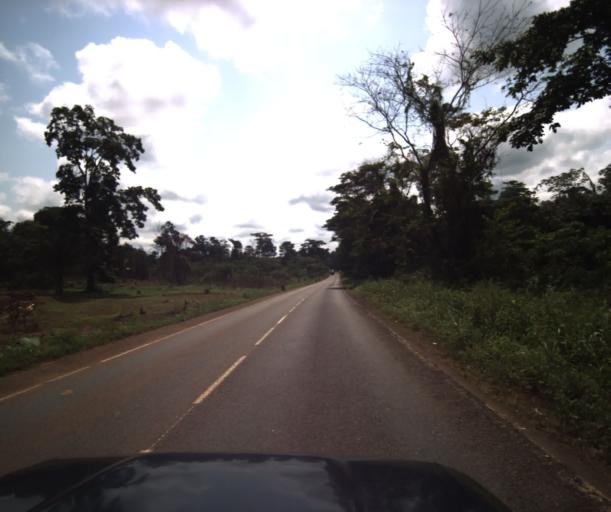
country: CM
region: Centre
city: Eseka
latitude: 3.8915
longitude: 10.7807
